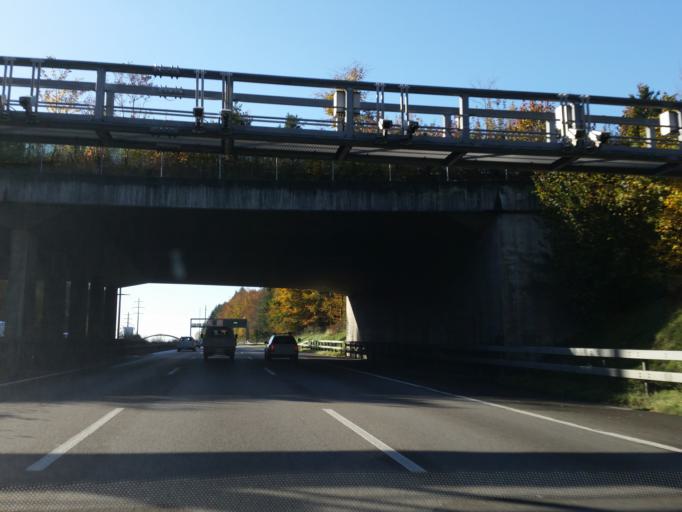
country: CH
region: Bern
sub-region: Bern-Mittelland District
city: Bolligen
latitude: 46.9985
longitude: 7.4876
